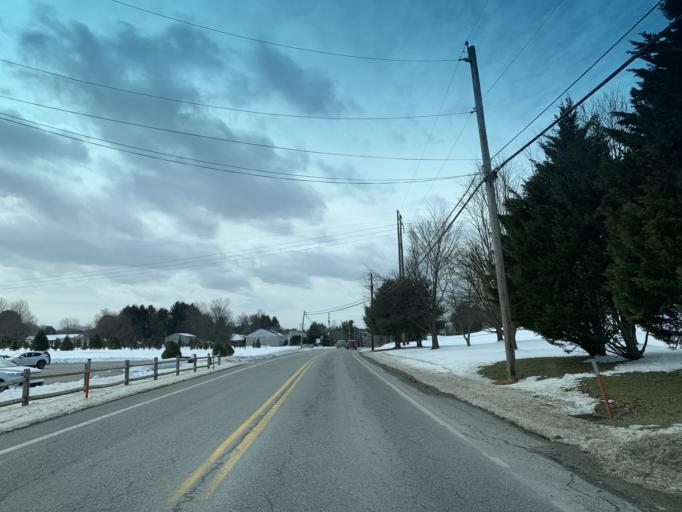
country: US
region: Pennsylvania
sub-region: York County
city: Shrewsbury
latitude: 39.7833
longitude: -76.6650
